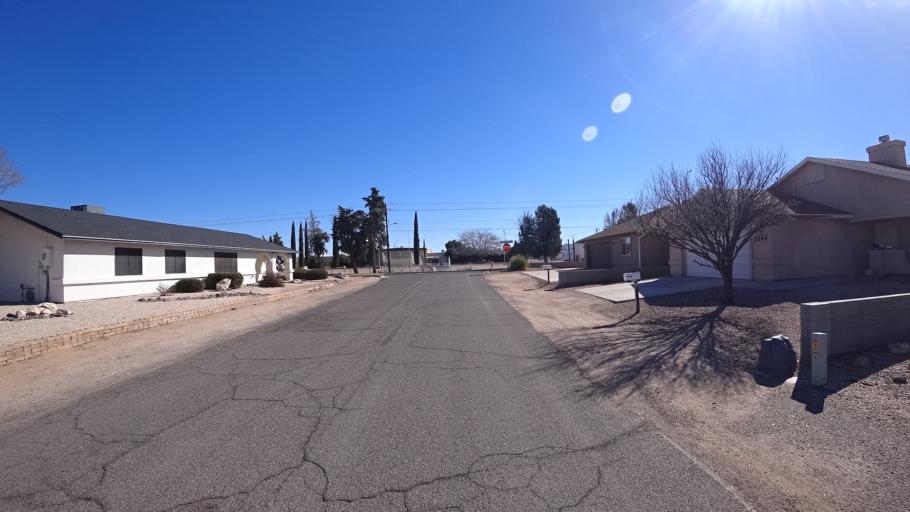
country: US
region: Arizona
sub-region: Mohave County
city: Kingman
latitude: 35.2112
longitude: -114.0296
